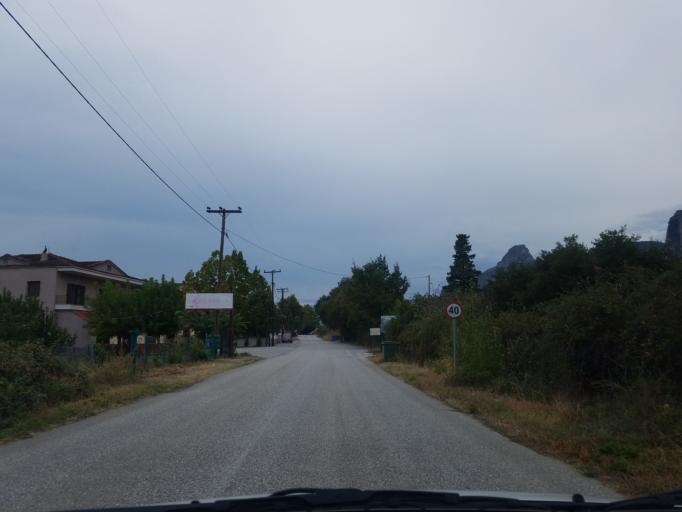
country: GR
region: Thessaly
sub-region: Trikala
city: Kalampaka
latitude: 39.6979
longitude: 21.6468
